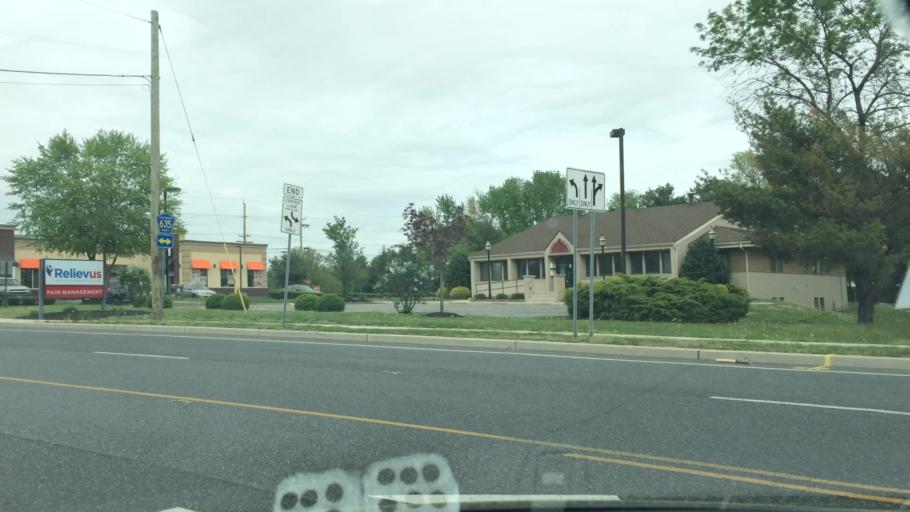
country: US
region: New Jersey
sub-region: Gloucester County
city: Turnersville
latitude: 39.7640
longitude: -75.0855
